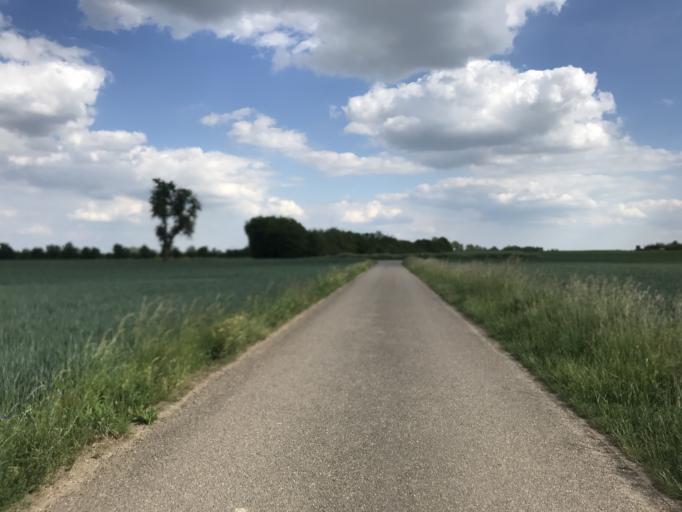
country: DE
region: Rheinland-Pfalz
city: Nieder-Ingelheim
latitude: 49.9739
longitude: 8.0929
